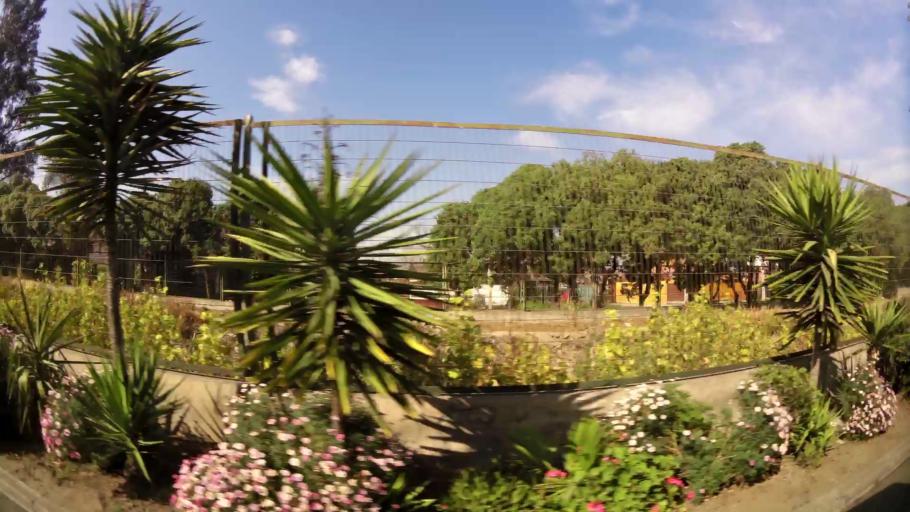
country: CL
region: Santiago Metropolitan
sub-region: Provincia de Santiago
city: Lo Prado
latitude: -33.4672
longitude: -70.7441
